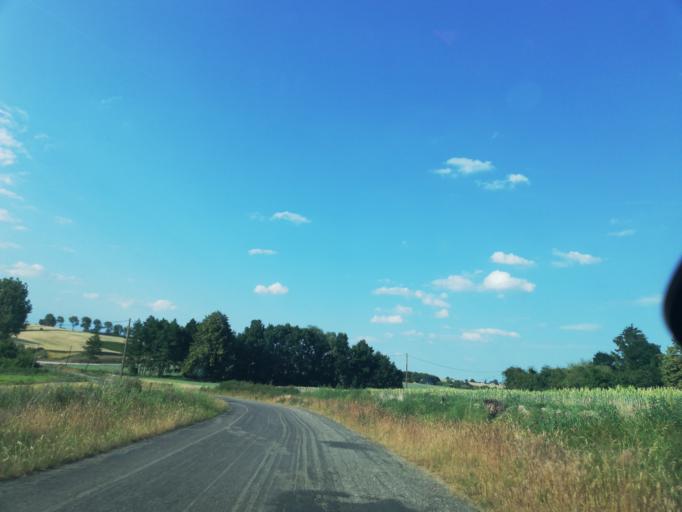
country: PL
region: Kujawsko-Pomorskie
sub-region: Powiat golubsko-dobrzynski
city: Golub-Dobrzyn
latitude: 53.0350
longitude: 19.0376
